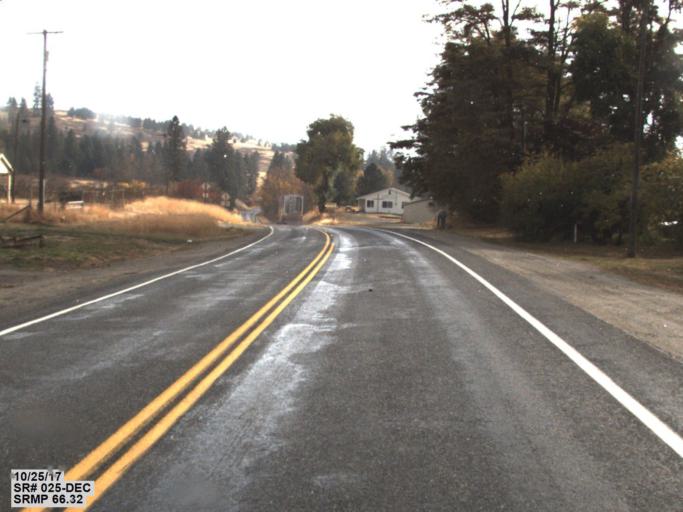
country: US
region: Washington
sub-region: Stevens County
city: Kettle Falls
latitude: 48.4285
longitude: -118.1708
